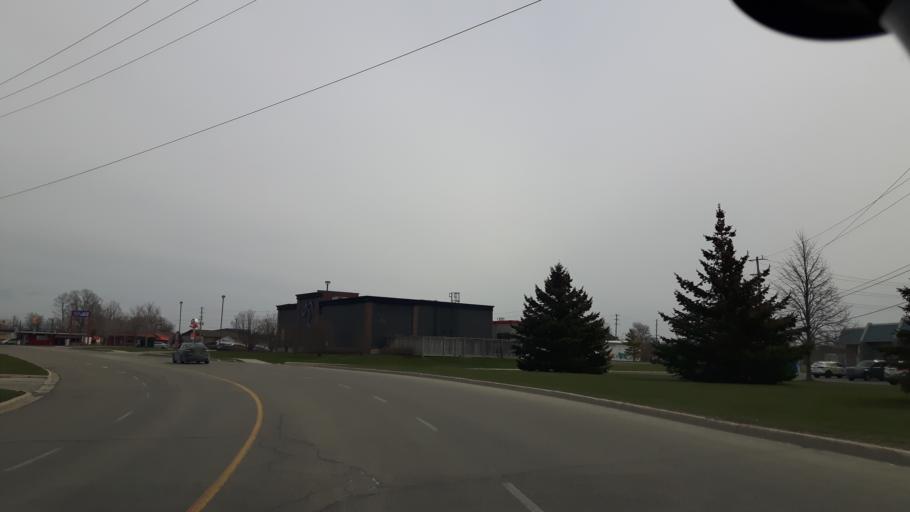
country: CA
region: Ontario
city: Goderich
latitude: 43.7317
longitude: -81.6953
